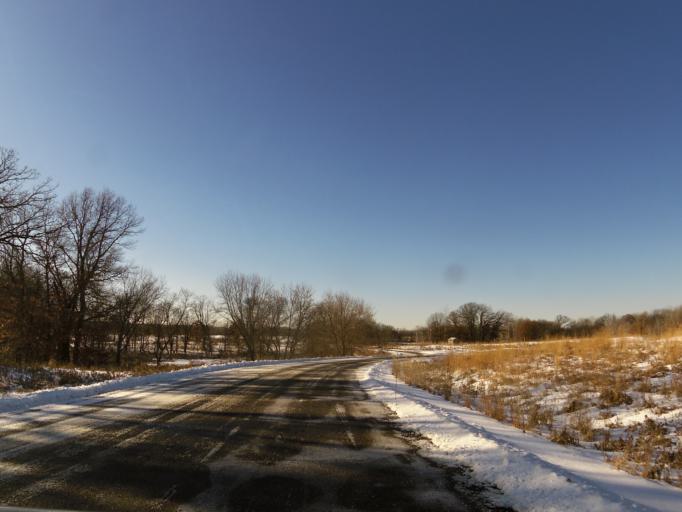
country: US
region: Minnesota
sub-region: Washington County
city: Lake Elmo
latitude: 44.9817
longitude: -92.9023
